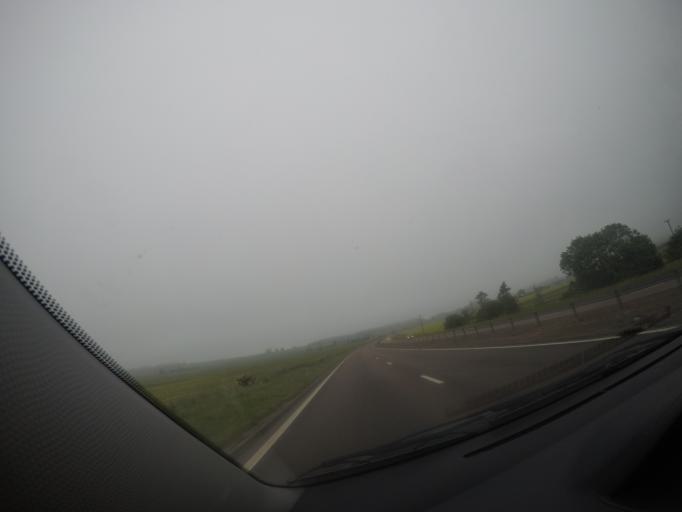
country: GB
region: Scotland
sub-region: Dundee City
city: Dundee
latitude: 56.5363
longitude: -2.9466
